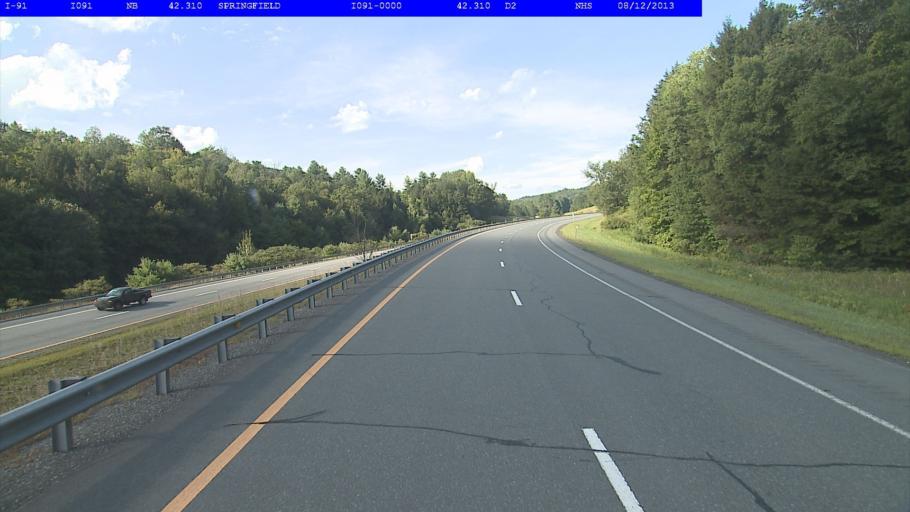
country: US
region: New Hampshire
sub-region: Sullivan County
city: Charlestown
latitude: 43.2755
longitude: -72.4346
